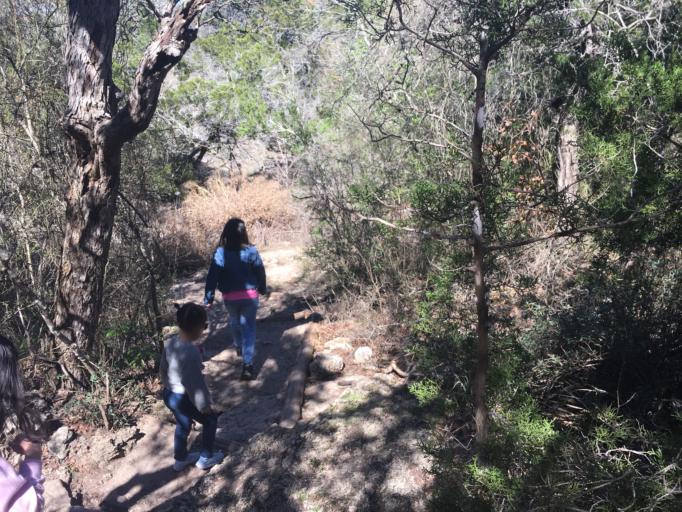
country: US
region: Texas
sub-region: Travis County
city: Briarcliff
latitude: 30.3424
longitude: -98.1293
